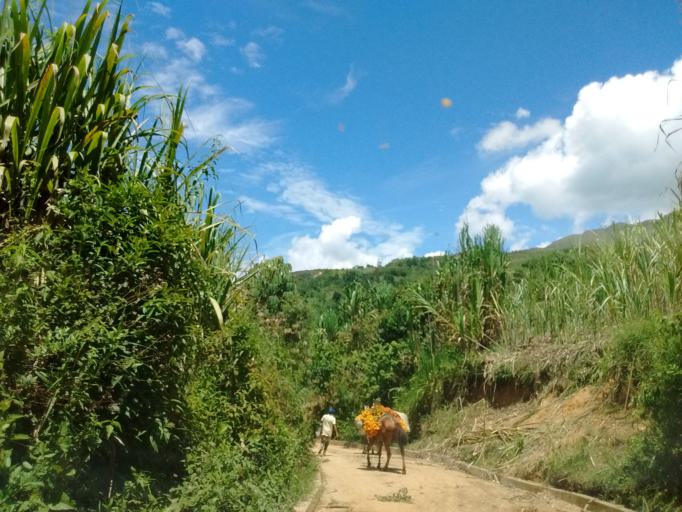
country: CO
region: Cauca
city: Villa Rica
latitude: 2.6289
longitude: -76.7722
